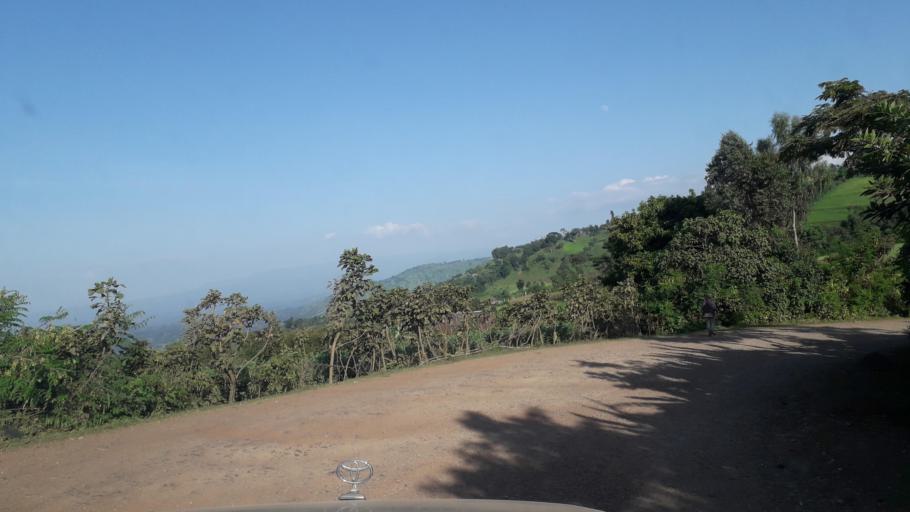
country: ET
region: Oromiya
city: Jima
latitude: 7.4666
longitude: 36.8753
